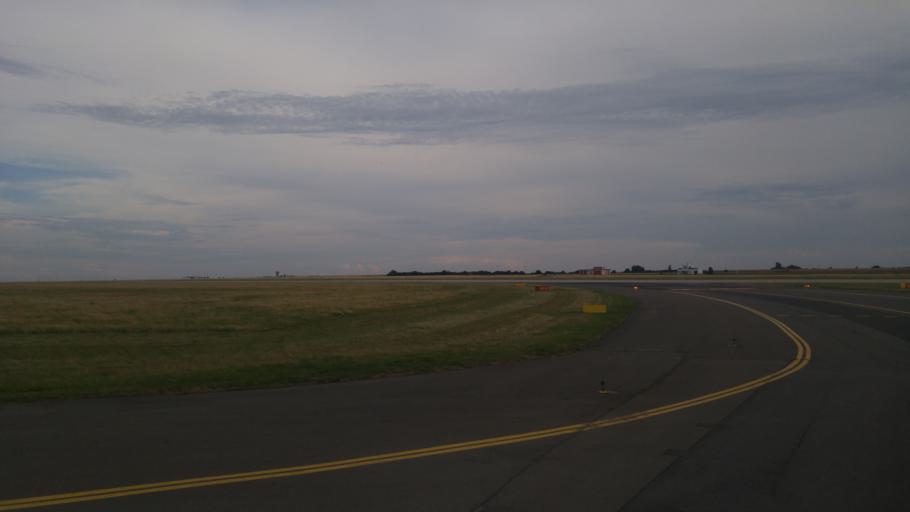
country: CZ
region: Central Bohemia
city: Hostivice
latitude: 50.1047
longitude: 14.2574
